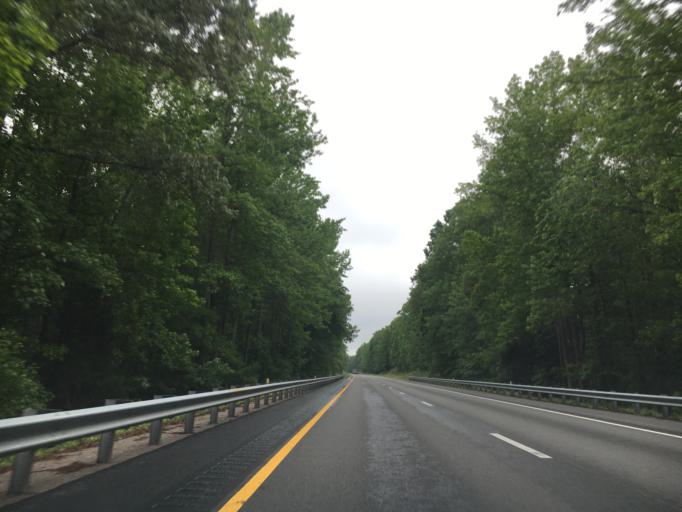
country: US
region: Virginia
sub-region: Dinwiddie County
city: Dinwiddie
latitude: 37.0515
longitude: -77.6103
